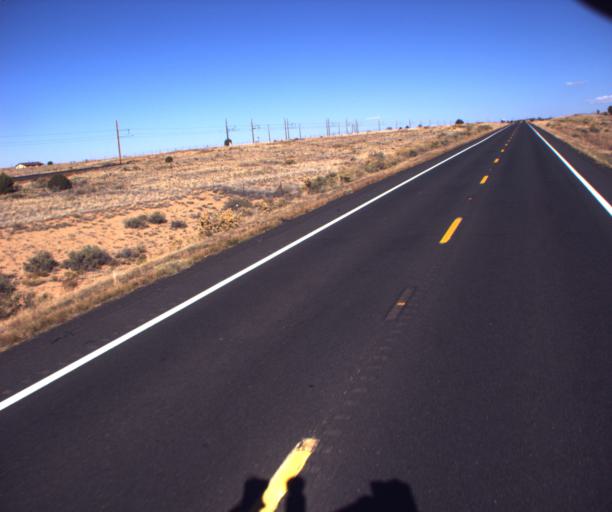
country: US
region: Arizona
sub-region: Coconino County
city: Kaibito
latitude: 36.4372
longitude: -110.7581
